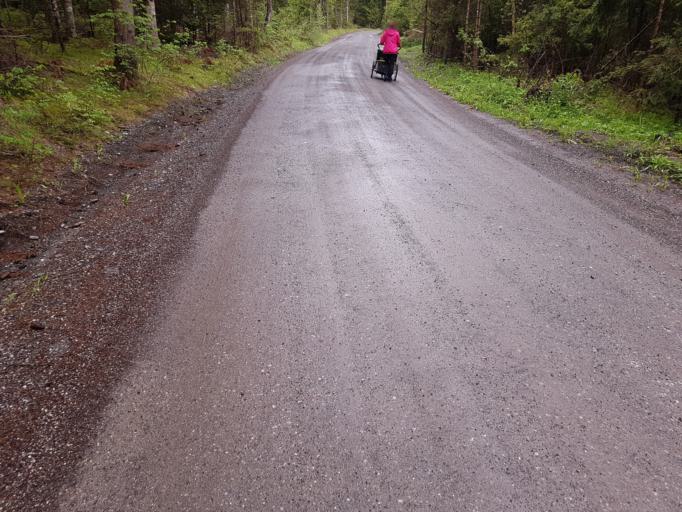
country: AT
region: Tyrol
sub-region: Politischer Bezirk Imst
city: Obsteig
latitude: 47.2937
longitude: 10.9127
